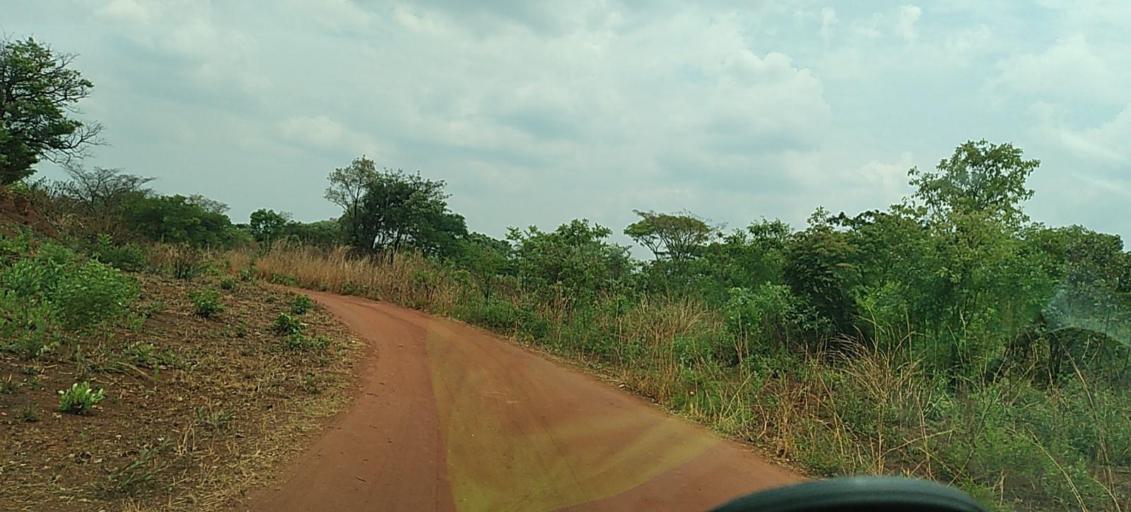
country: ZM
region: North-Western
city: Kansanshi
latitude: -12.0465
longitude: 26.3817
